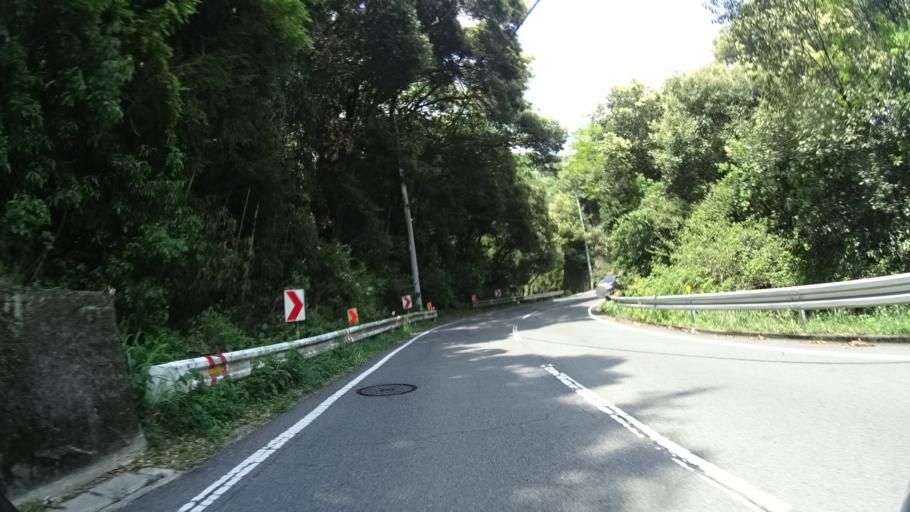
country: JP
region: Ehime
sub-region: Shikoku-chuo Shi
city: Matsuyama
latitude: 33.8724
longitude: 132.8307
